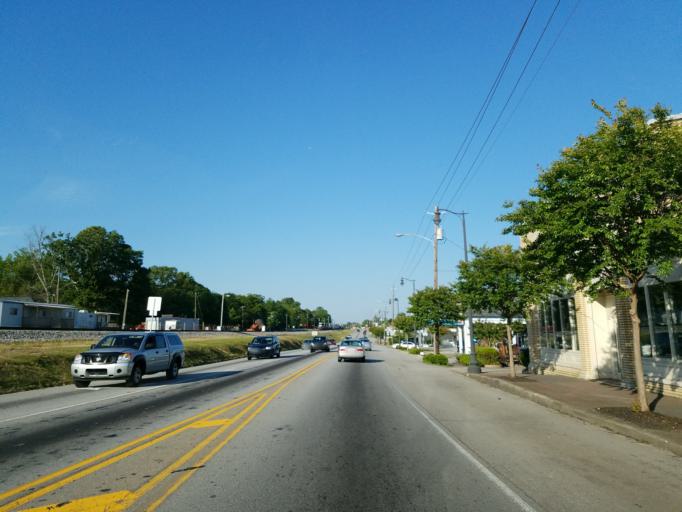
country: US
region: Georgia
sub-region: Douglas County
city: Douglasville
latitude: 33.7518
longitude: -84.7471
